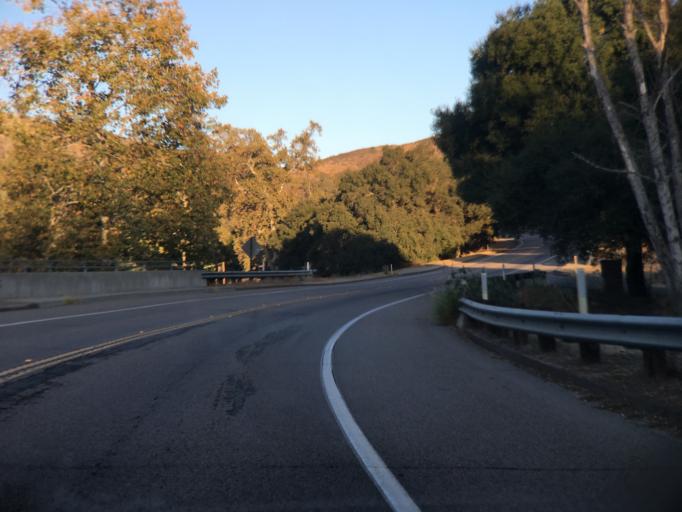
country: US
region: California
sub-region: San Diego County
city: Harbison Canyon
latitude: 32.8035
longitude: -116.8201
